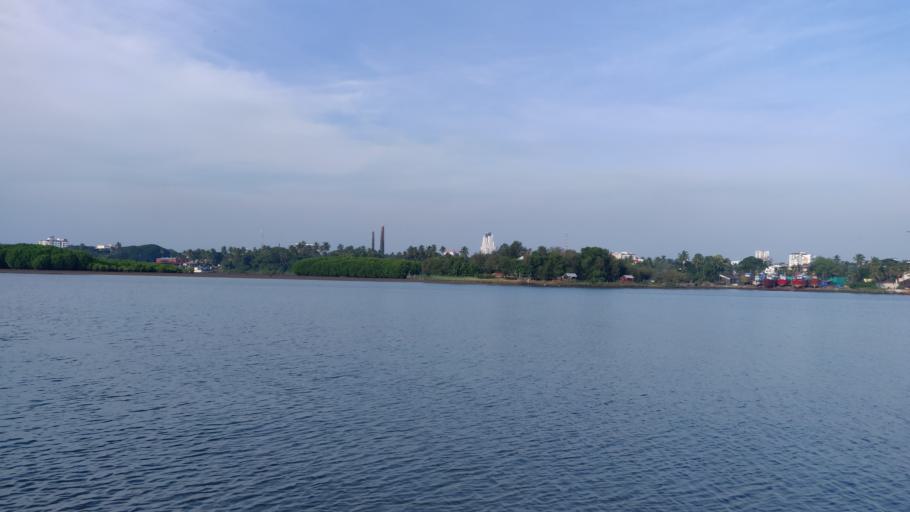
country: IN
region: Karnataka
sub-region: Dakshina Kannada
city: Mangalore
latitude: 12.8755
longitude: 74.8242
